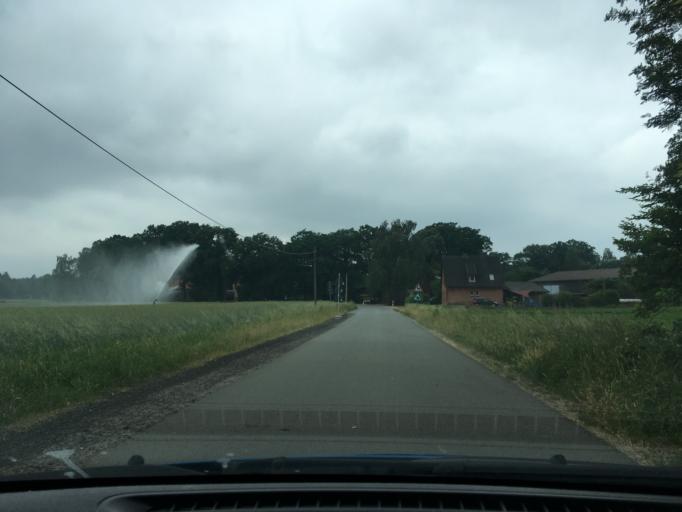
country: DE
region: Lower Saxony
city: Zernien
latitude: 53.0929
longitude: 10.8868
